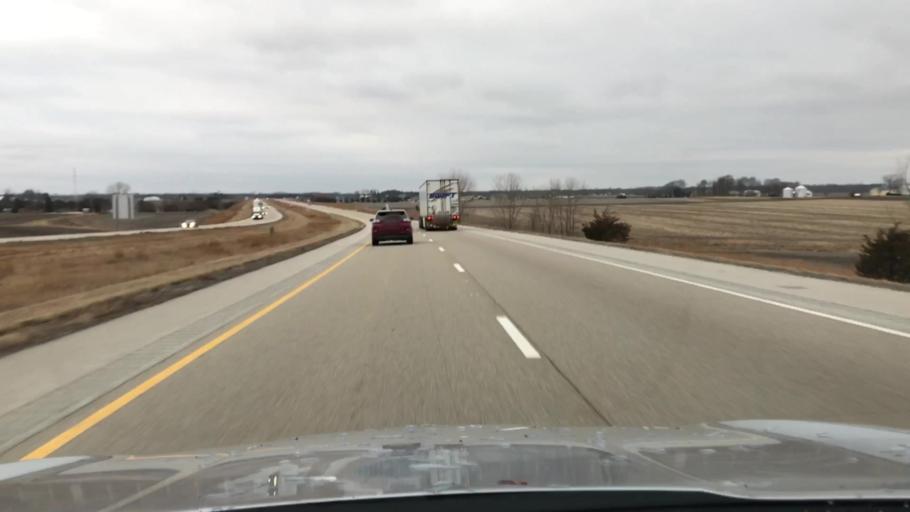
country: US
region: Illinois
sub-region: Logan County
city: Lincoln
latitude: 40.1853
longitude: -89.3239
